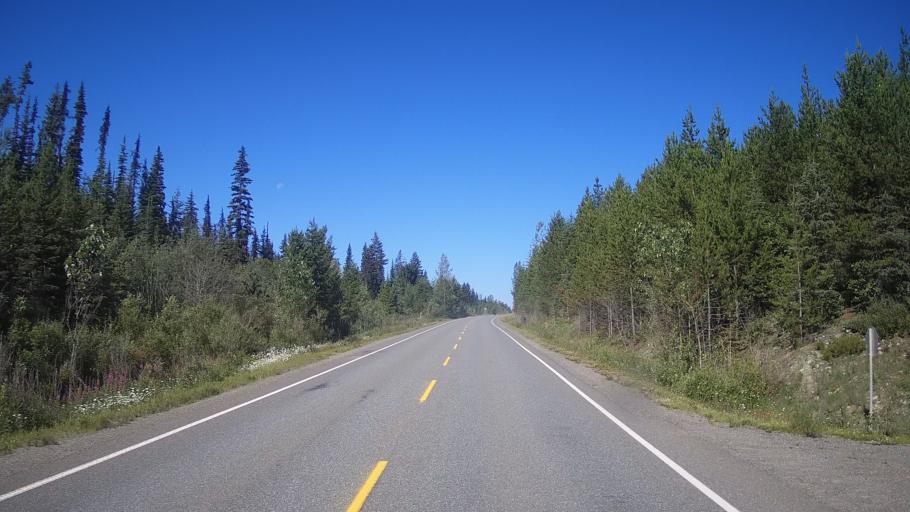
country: CA
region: British Columbia
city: Kamloops
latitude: 51.4965
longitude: -120.3882
